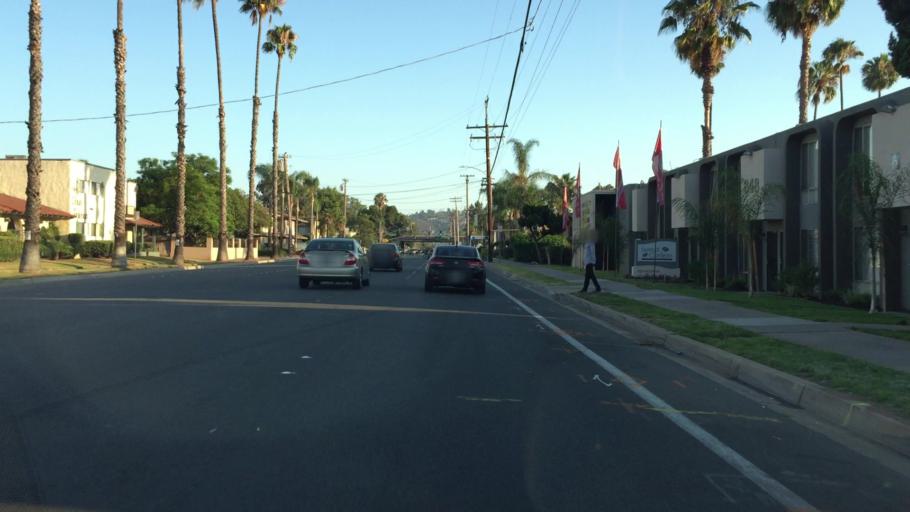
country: US
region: California
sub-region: San Diego County
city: Bostonia
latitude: 32.8067
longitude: -116.9511
